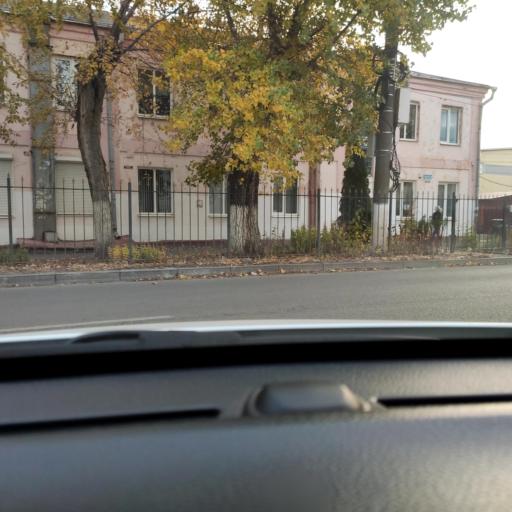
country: RU
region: Voronezj
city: Voronezh
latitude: 51.6850
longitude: 39.1729
